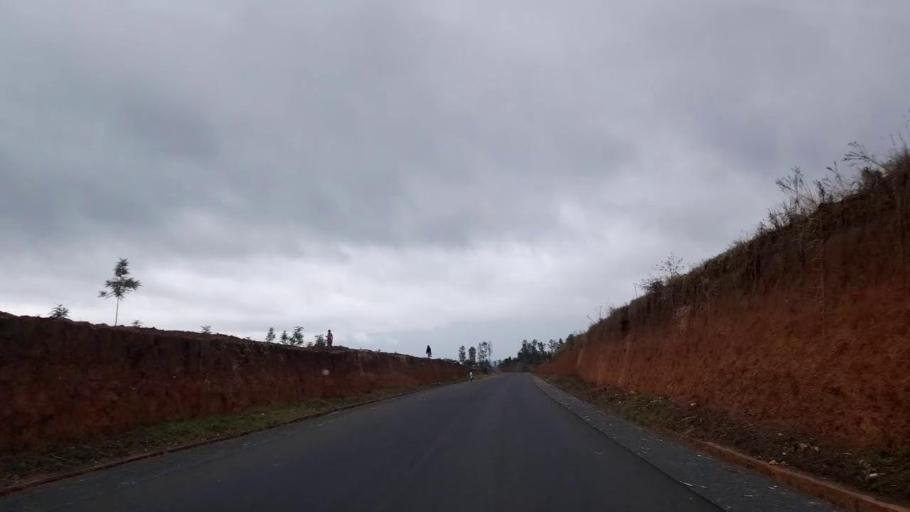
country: RW
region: Northern Province
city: Byumba
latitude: -1.4346
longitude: 30.2599
